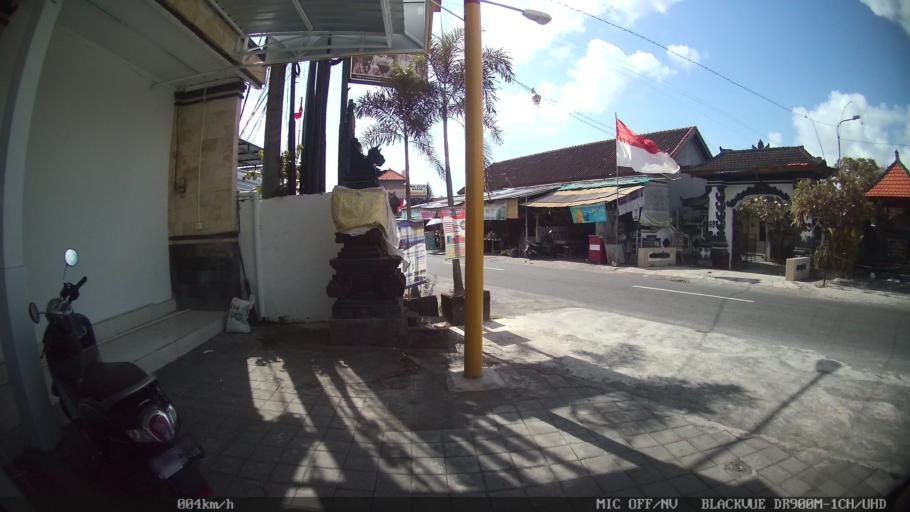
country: ID
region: Bali
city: Jabajero
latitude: -8.7195
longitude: 115.1922
